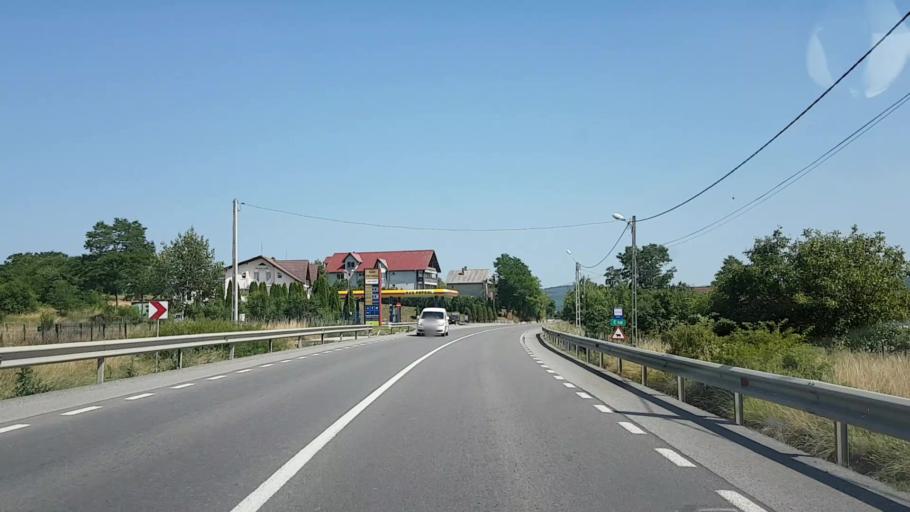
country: RO
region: Bistrita-Nasaud
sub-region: Comuna Uriu
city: Cristestii Ciceului
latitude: 47.1816
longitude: 24.1382
